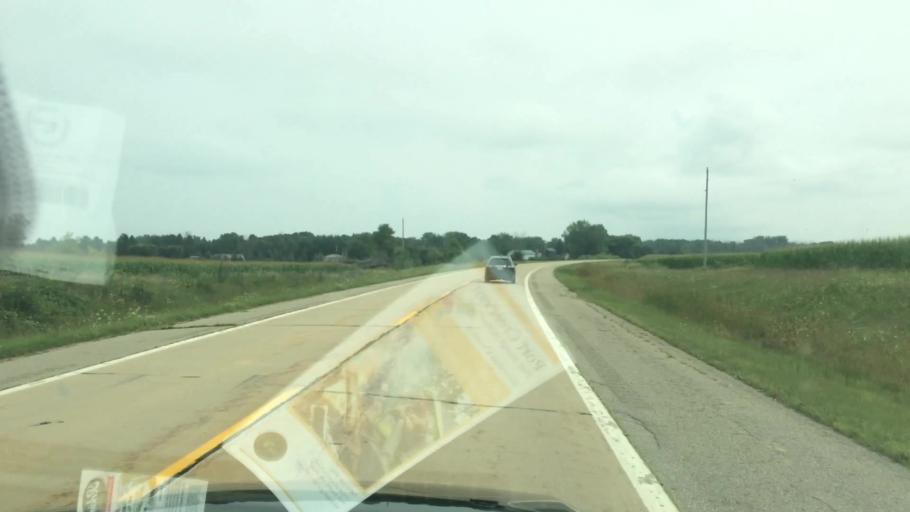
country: US
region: Michigan
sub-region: Huron County
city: Bad Axe
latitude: 44.0444
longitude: -82.8866
